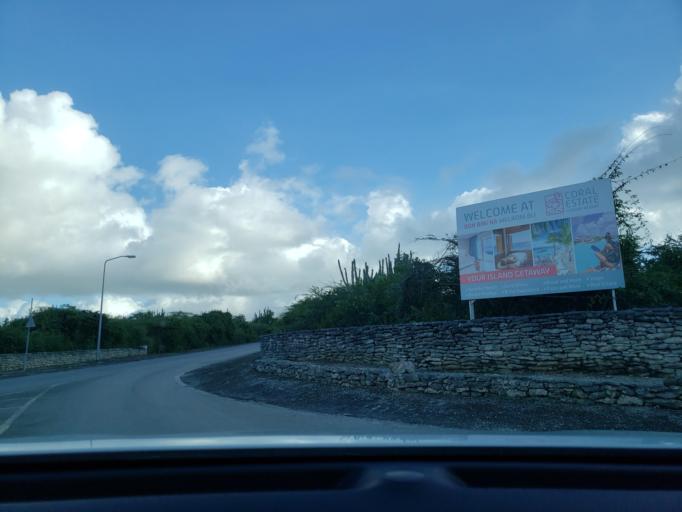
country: CW
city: Dorp Soto
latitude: 12.2133
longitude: -69.0720
